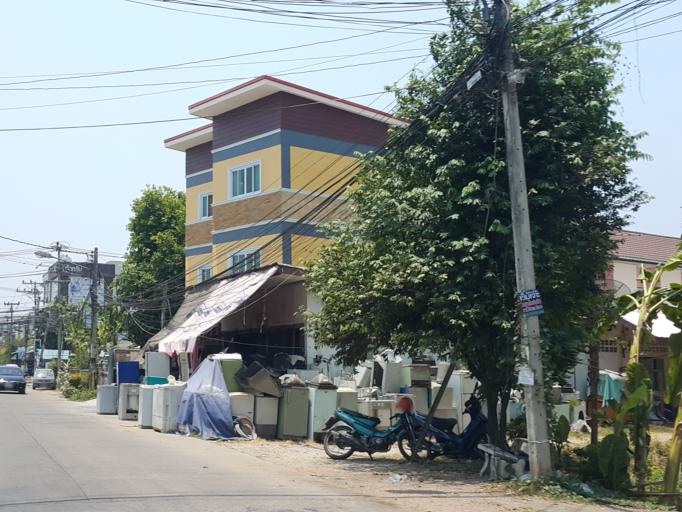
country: TH
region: Phitsanulok
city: Phitsanulok
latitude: 16.8168
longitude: 100.2571
